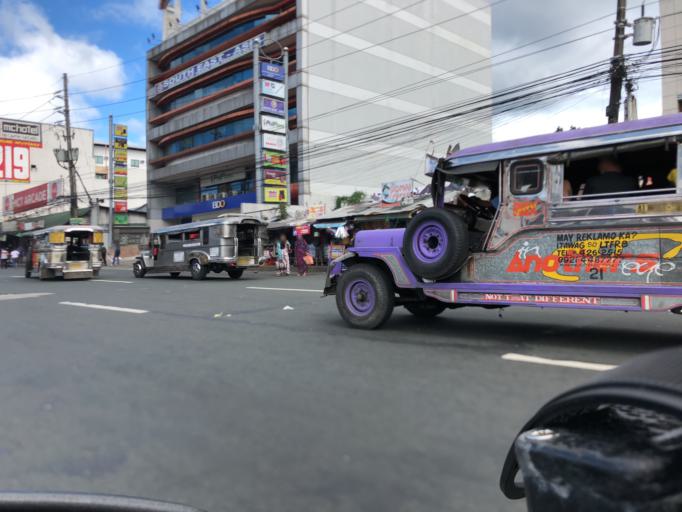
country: PH
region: Calabarzon
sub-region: Province of Rizal
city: San Mateo
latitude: 14.7331
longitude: 121.0612
